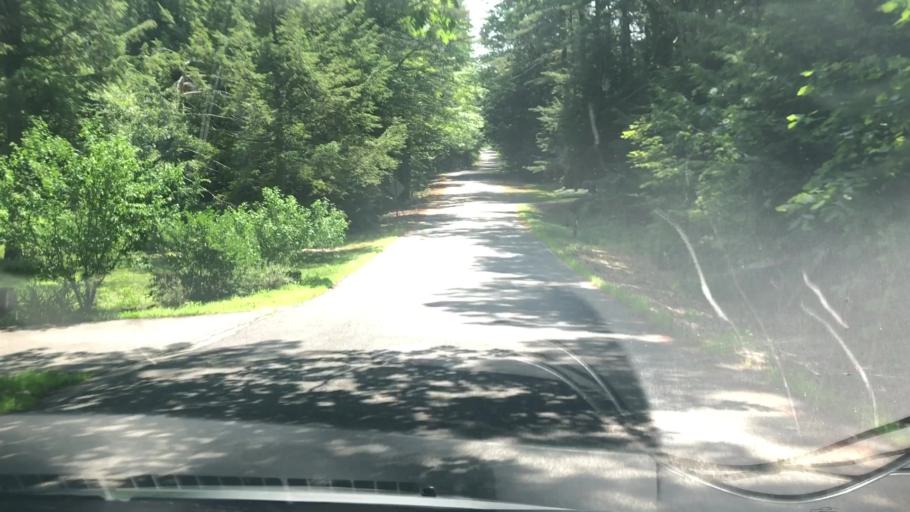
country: US
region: New Hampshire
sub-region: Hillsborough County
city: Milford
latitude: 42.8769
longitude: -71.6333
